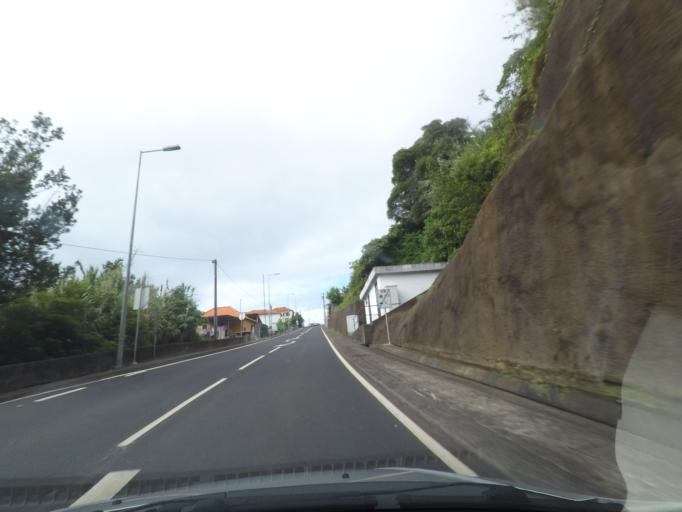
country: PT
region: Madeira
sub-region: Santana
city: Santana
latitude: 32.8185
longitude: -16.8906
